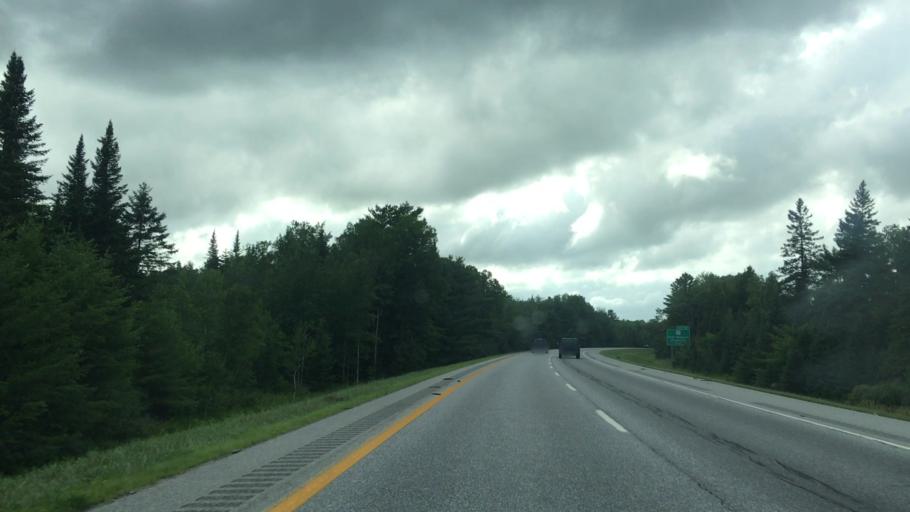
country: US
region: Maine
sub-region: Penobscot County
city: Plymouth
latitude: 44.7921
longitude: -69.2016
